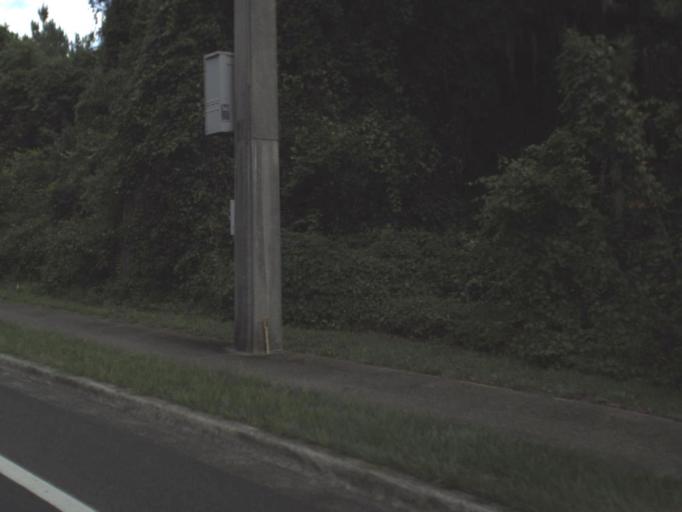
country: US
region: Florida
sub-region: Alachua County
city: Alachua
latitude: 29.6888
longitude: -82.4292
